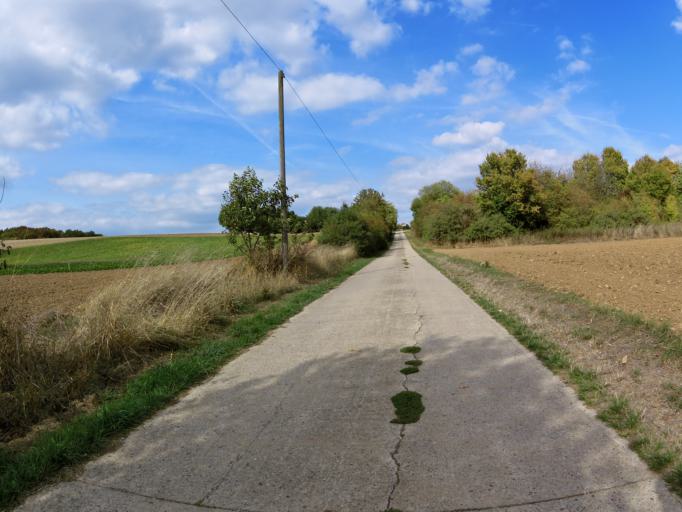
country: DE
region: Bavaria
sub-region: Regierungsbezirk Unterfranken
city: Hettstadt
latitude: 49.7862
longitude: 9.7946
